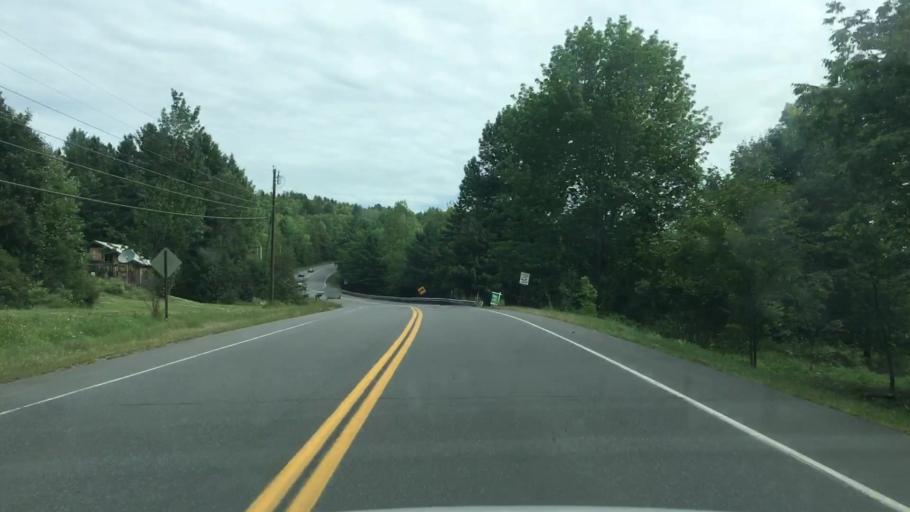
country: US
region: Maine
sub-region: Piscataquis County
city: Dover-Foxcroft
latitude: 45.2120
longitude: -69.1714
